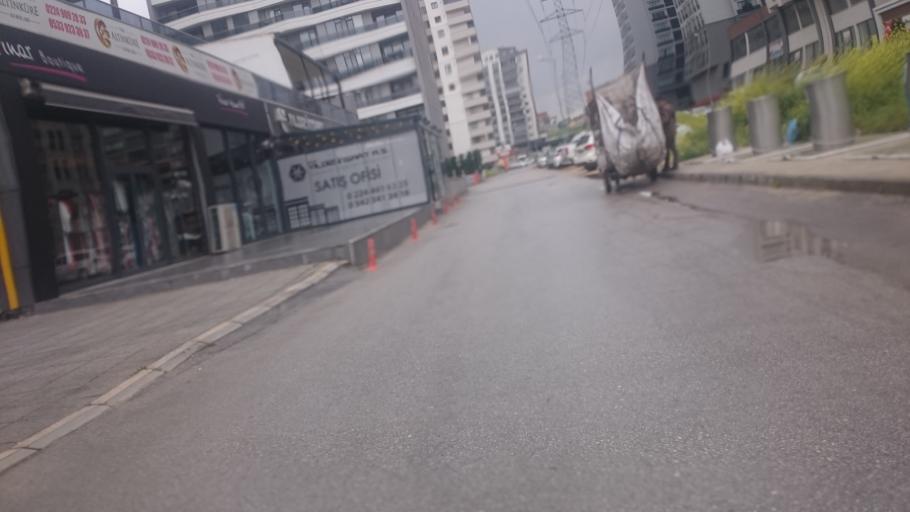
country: TR
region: Bursa
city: Cali
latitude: 40.2179
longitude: 28.9426
